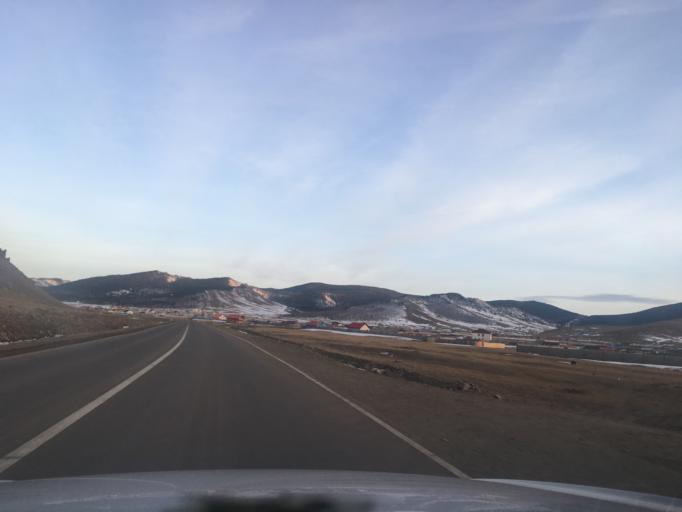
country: MN
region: Ulaanbaatar
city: Ulaanbaatar
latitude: 48.0974
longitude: 106.7403
